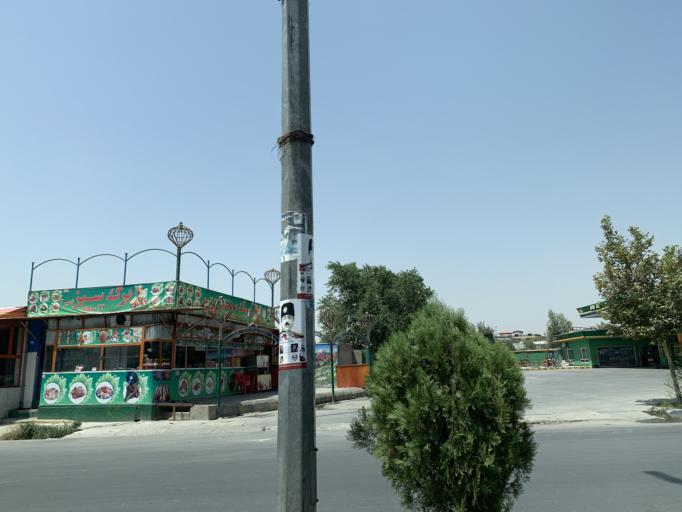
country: AF
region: Kabul
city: Kabul
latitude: 34.5001
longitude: 69.1569
